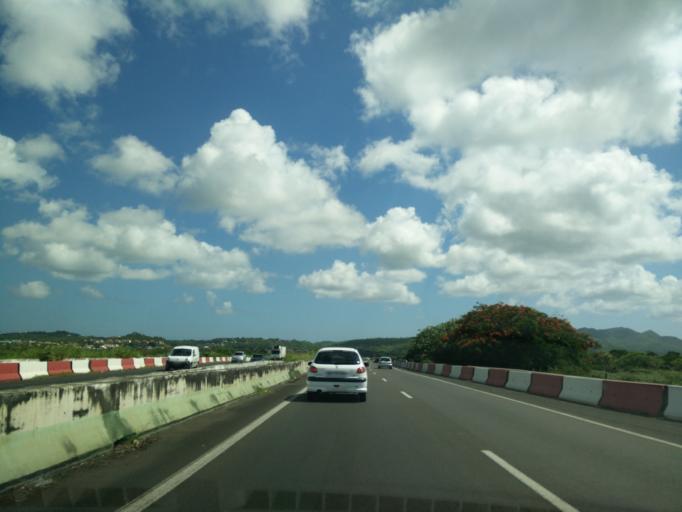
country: MQ
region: Martinique
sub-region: Martinique
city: Ducos
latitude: 14.5441
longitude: -60.9757
